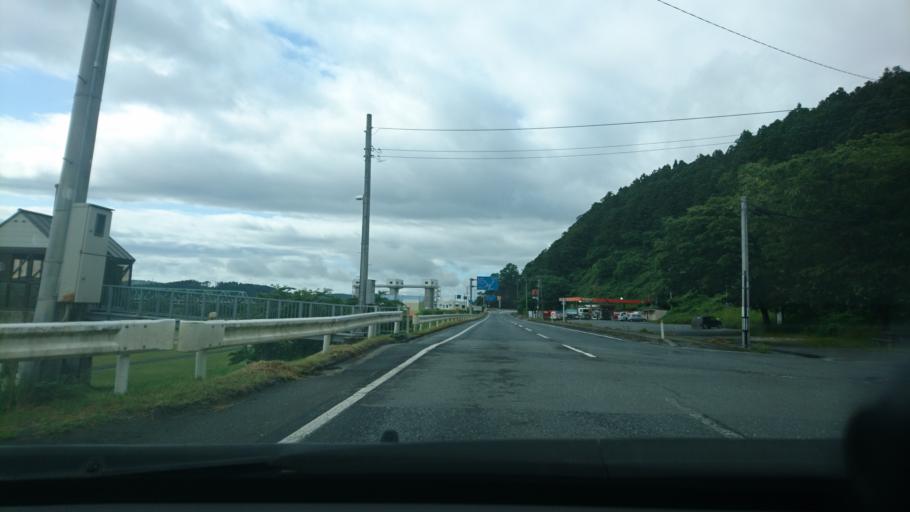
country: JP
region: Miyagi
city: Wakuya
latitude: 38.6005
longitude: 141.3032
